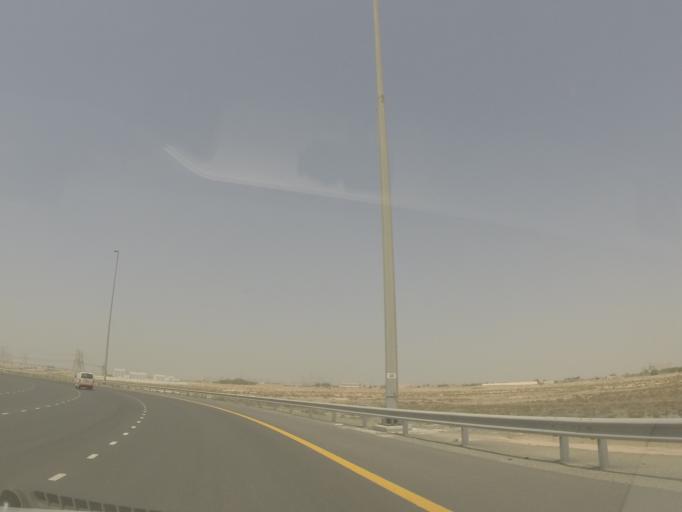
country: AE
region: Dubai
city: Dubai
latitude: 25.0046
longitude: 55.1749
